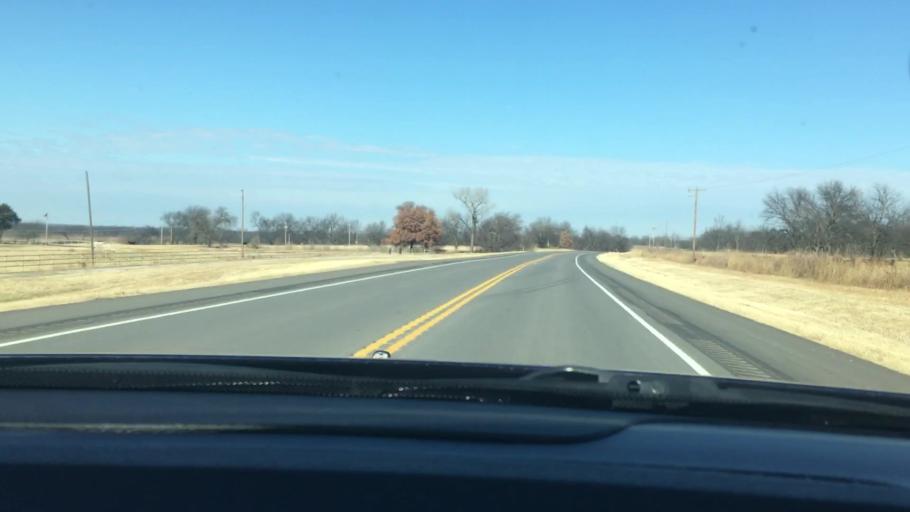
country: US
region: Oklahoma
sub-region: Murray County
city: Davis
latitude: 34.5465
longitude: -97.1312
